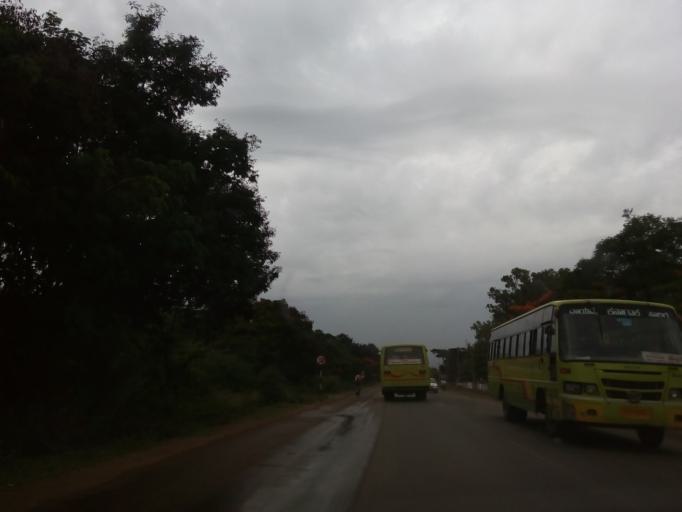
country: IN
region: Karnataka
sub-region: Davanagere
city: Harihar
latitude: 14.5243
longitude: 75.7827
